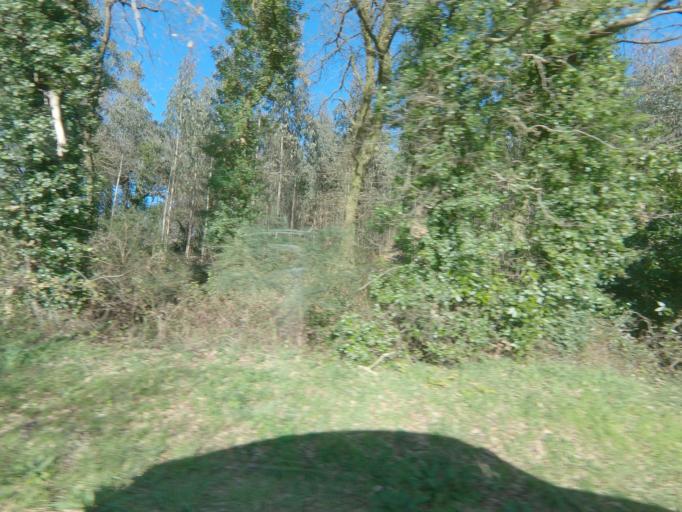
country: ES
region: Galicia
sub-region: Provincia da Coruna
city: Ribeira
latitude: 42.7107
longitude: -8.4315
